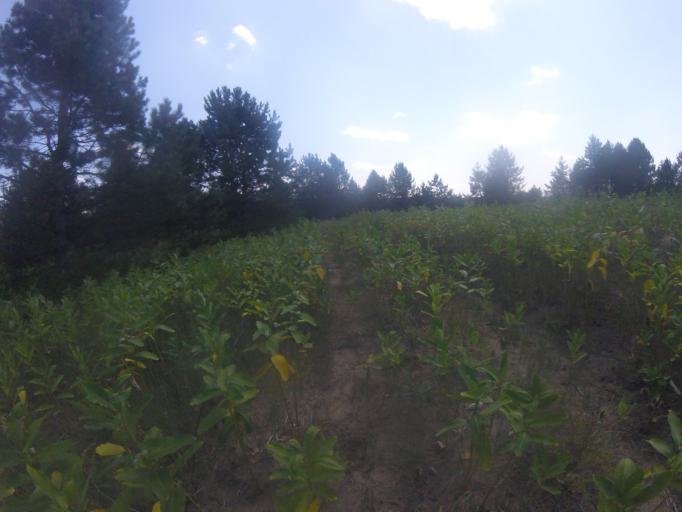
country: HU
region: Bacs-Kiskun
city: Jaszszentlaszlo
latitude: 46.6082
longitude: 19.7144
